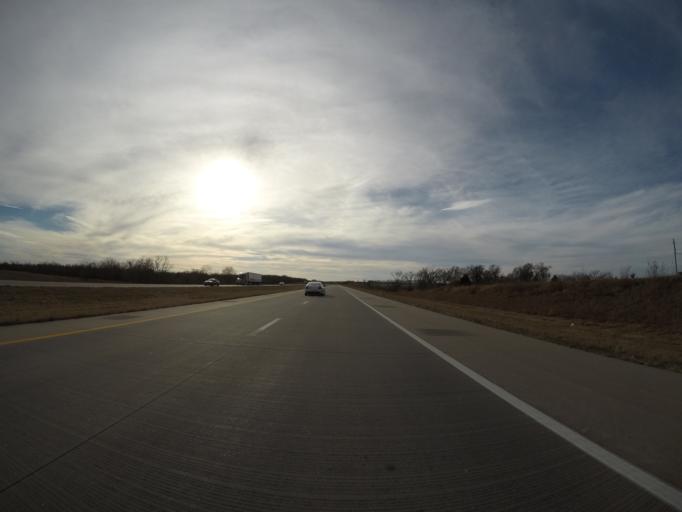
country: US
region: Kansas
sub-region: Franklin County
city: Wellsville
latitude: 38.6663
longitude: -95.1669
